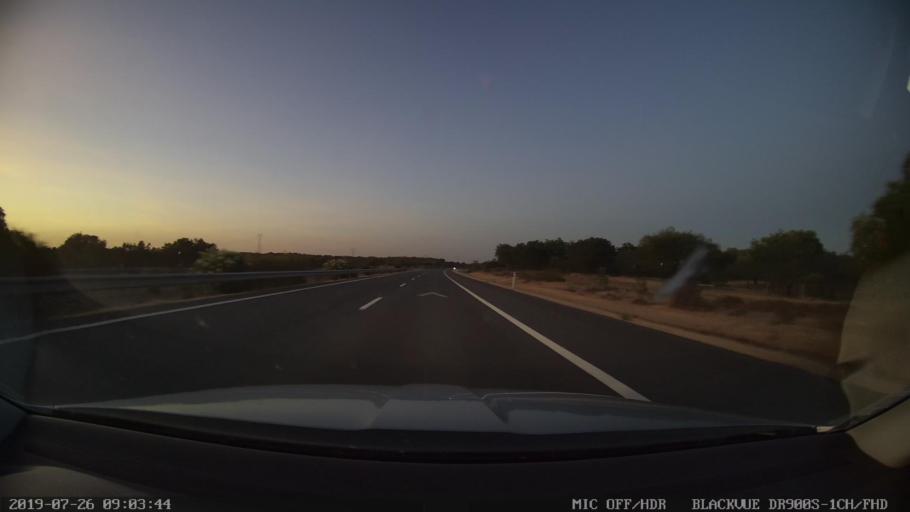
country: PT
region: Evora
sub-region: Evora
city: Evora
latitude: 38.7001
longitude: -7.8035
